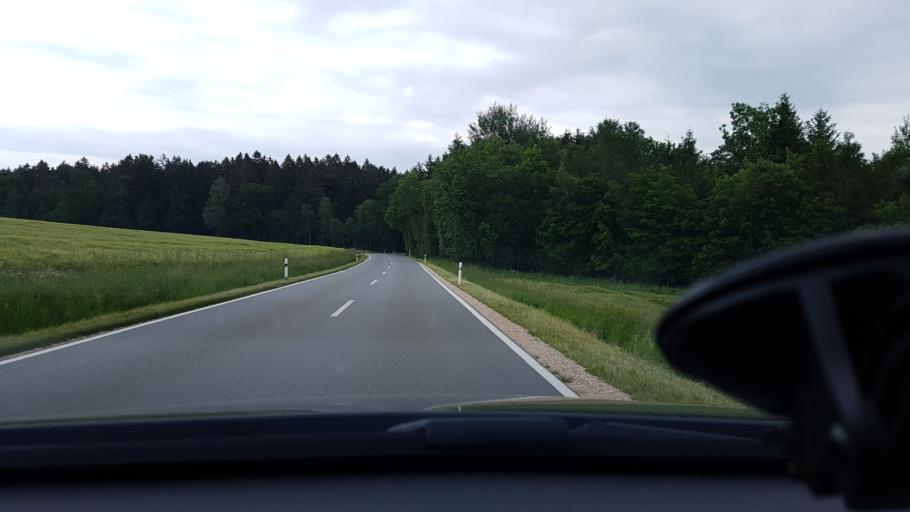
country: DE
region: Bavaria
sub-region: Lower Bavaria
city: Stubenberg
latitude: 48.3398
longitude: 13.0456
